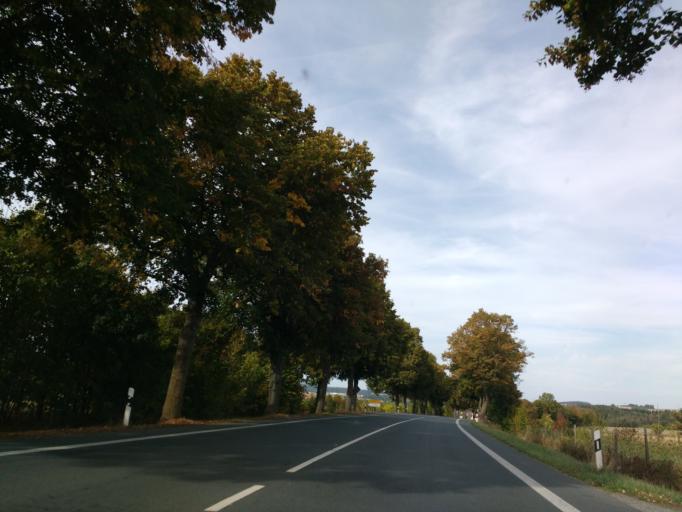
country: DE
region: North Rhine-Westphalia
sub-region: Regierungsbezirk Detmold
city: Willebadessen
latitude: 51.6141
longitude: 9.1342
